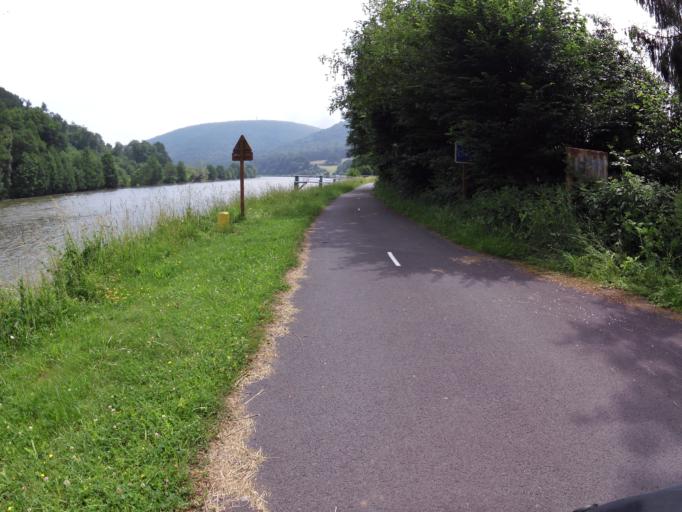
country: FR
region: Champagne-Ardenne
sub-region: Departement des Ardennes
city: Vireux-Wallerand
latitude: 50.0931
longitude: 4.7397
